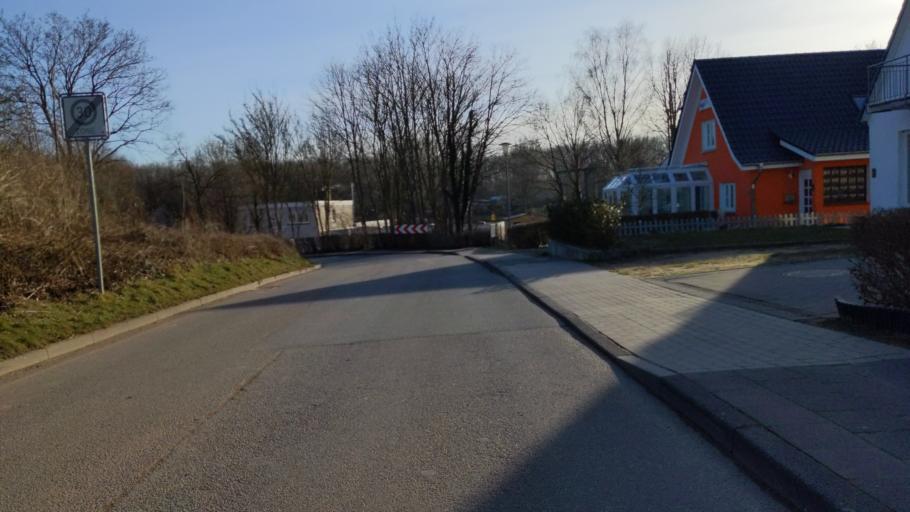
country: DE
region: Schleswig-Holstein
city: Scharbeutz
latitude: 54.0306
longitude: 10.7414
